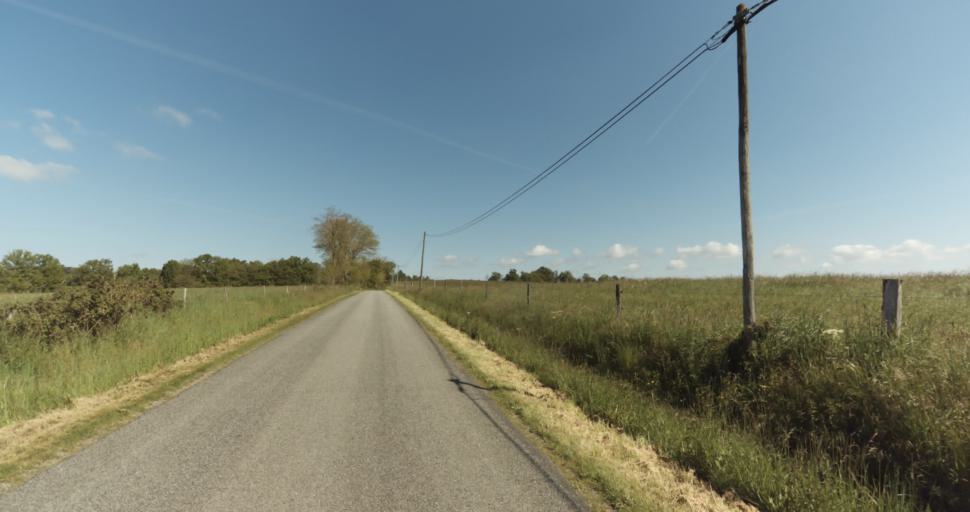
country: FR
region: Limousin
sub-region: Departement de la Haute-Vienne
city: Le Vigen
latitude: 45.7036
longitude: 1.3018
